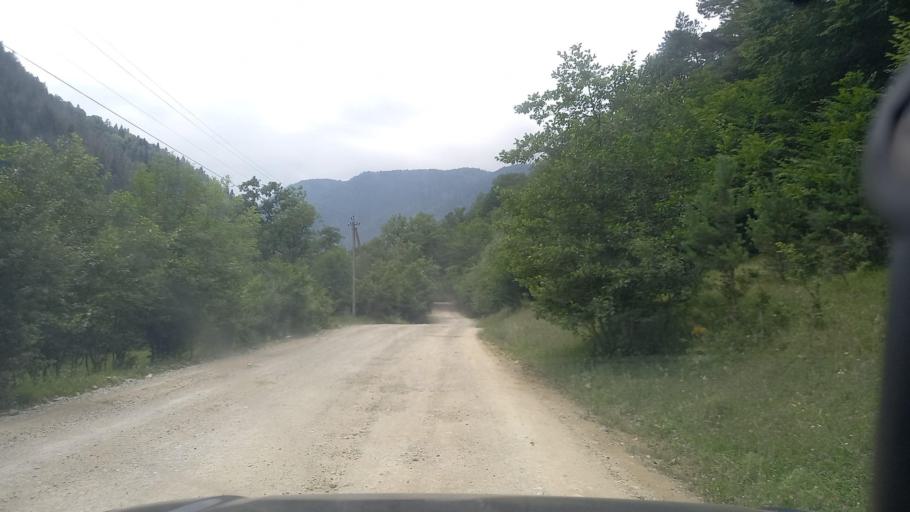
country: RU
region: Karachayevo-Cherkesiya
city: Kurdzhinovo
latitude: 43.9116
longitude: 40.9571
